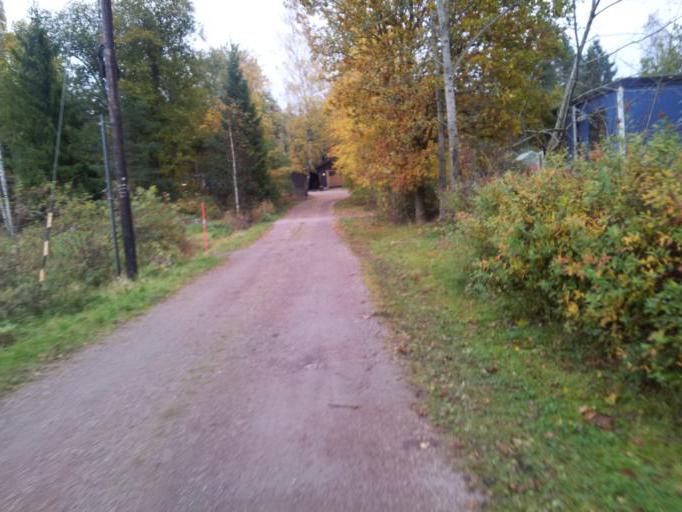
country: SE
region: Uppsala
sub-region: Uppsala Kommun
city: Storvreta
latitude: 59.9084
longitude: 17.7262
